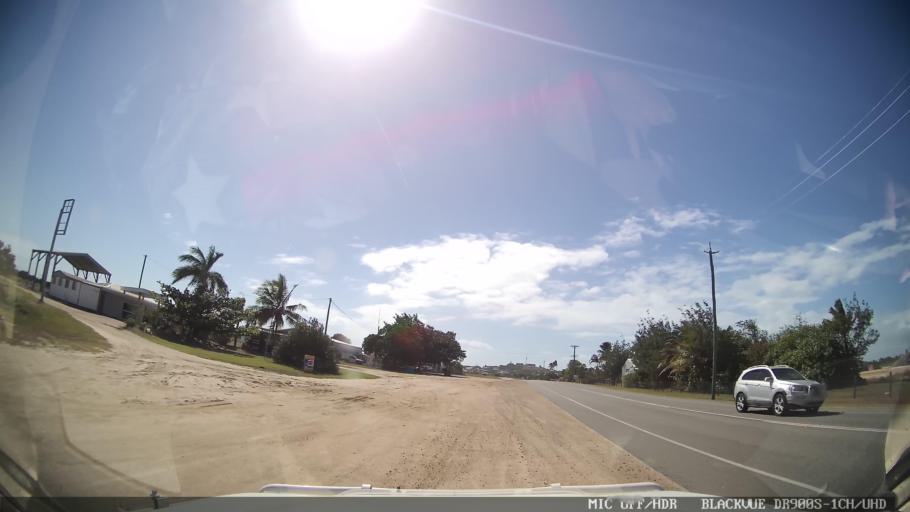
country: AU
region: Queensland
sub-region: Whitsunday
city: Bowen
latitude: -20.0134
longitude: 148.2238
